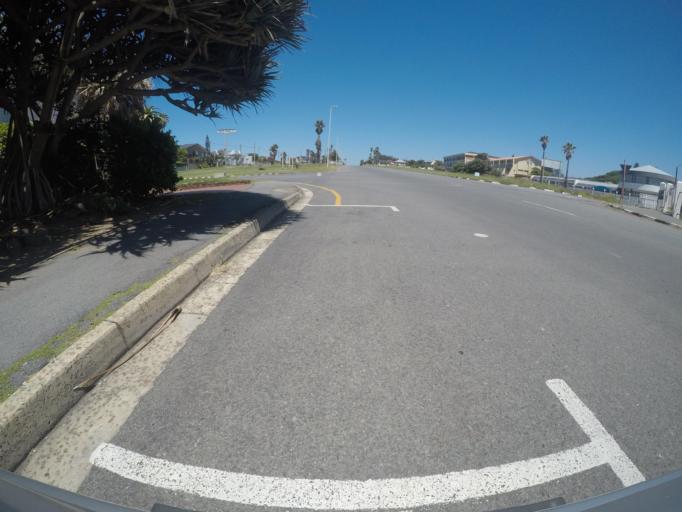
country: ZA
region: Eastern Cape
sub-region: Buffalo City Metropolitan Municipality
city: East London
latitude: -32.9393
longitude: 28.0317
